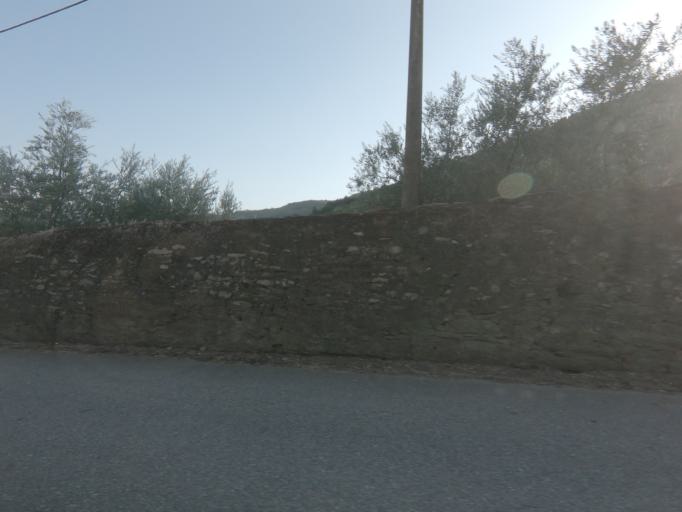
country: PT
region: Vila Real
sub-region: Sabrosa
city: Vilela
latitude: 41.1794
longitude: -7.5797
